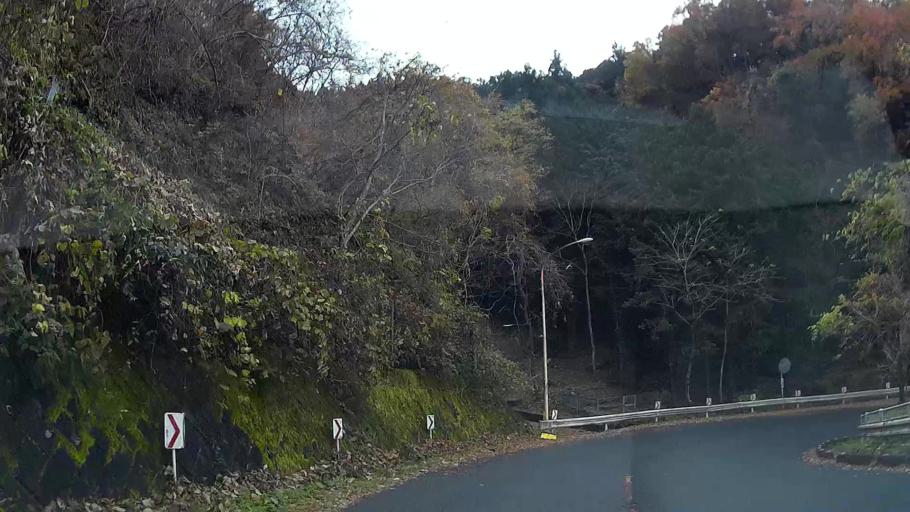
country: JP
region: Saitama
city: Chichibu
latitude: 35.9570
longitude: 139.0554
